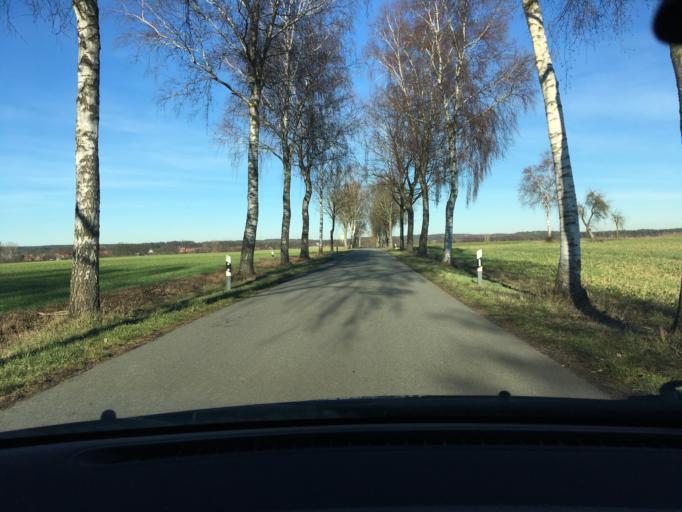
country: DE
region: Lower Saxony
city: Hanstedt Eins
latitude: 53.0374
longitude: 10.3712
